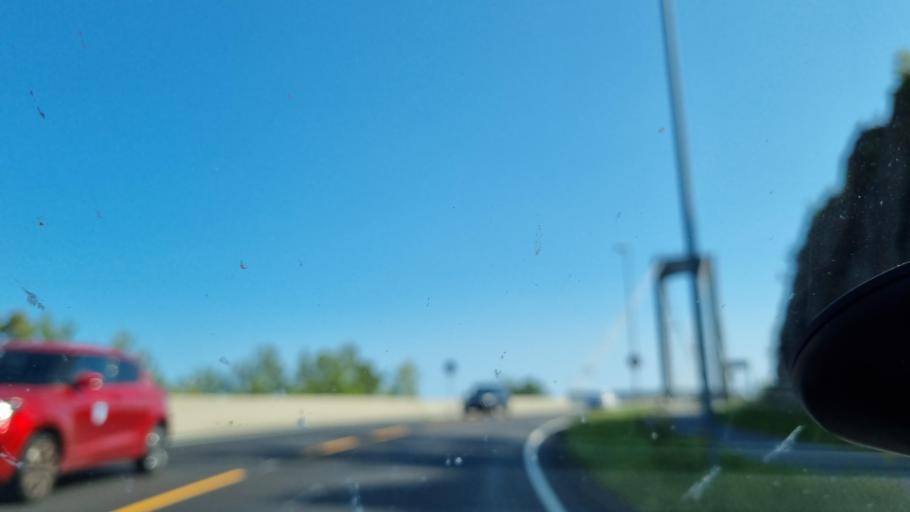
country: NO
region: Aust-Agder
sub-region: Arendal
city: Arendal
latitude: 58.4735
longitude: 8.8210
